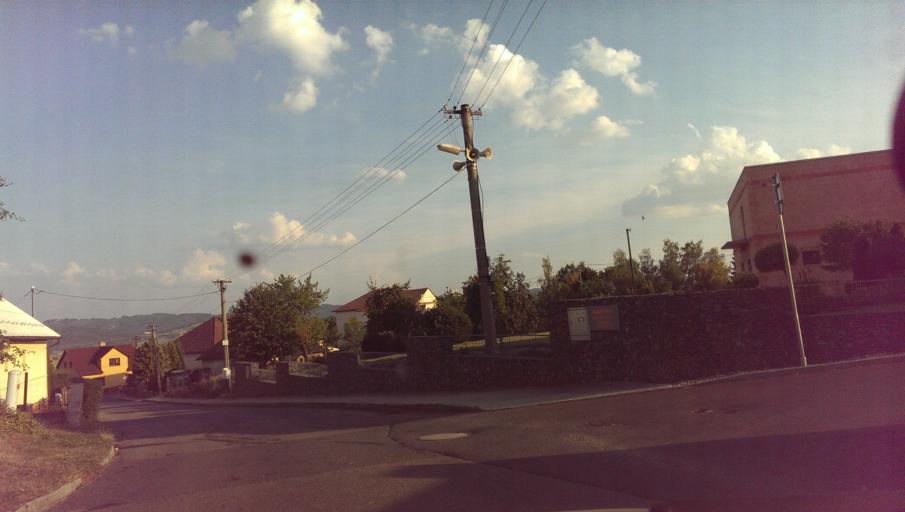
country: CZ
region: Zlin
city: Hvozdna
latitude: 49.2379
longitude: 17.7729
